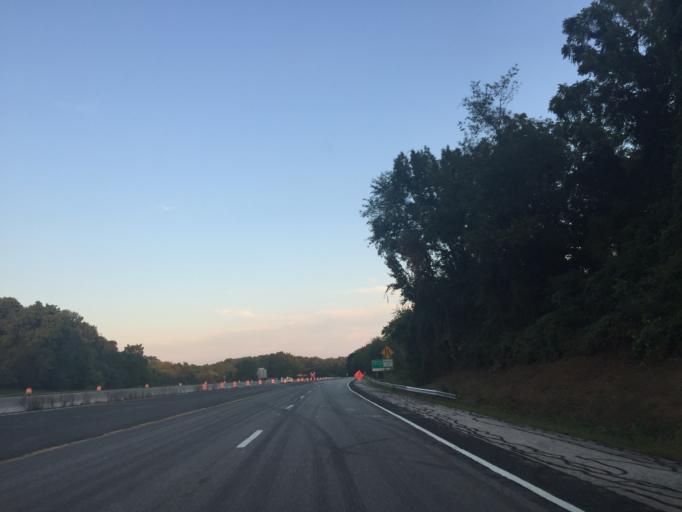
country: US
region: Maryland
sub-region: Baltimore County
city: Woodlawn
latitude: 39.3034
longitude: -76.7211
